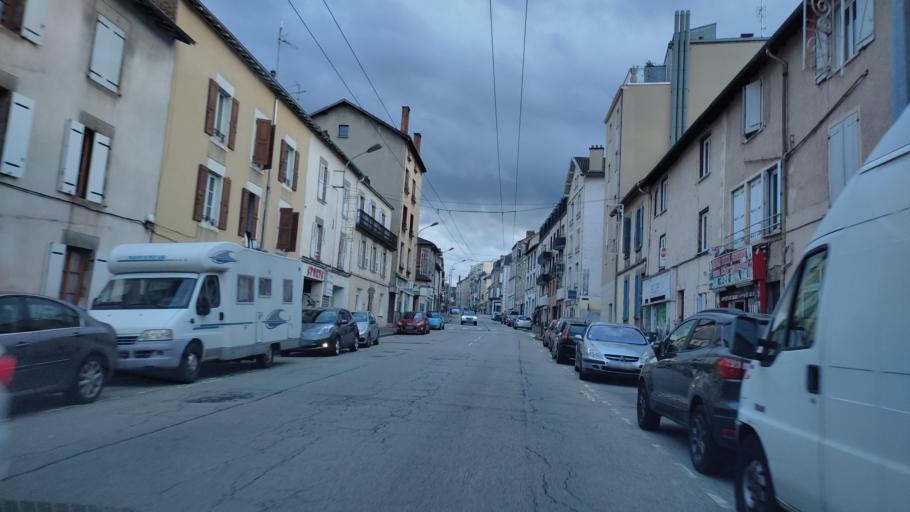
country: FR
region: Limousin
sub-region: Departement de la Haute-Vienne
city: Limoges
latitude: 45.8387
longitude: 1.2569
